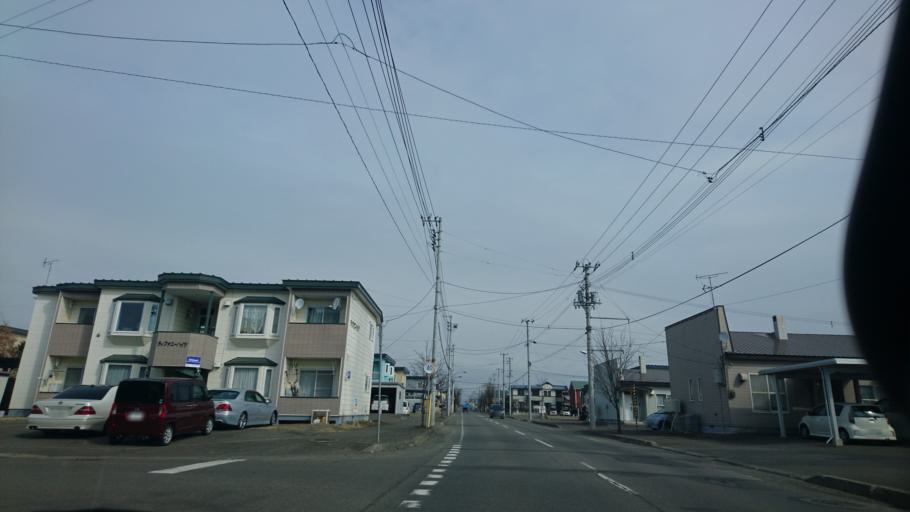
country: JP
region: Hokkaido
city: Otofuke
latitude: 42.9643
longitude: 143.2134
